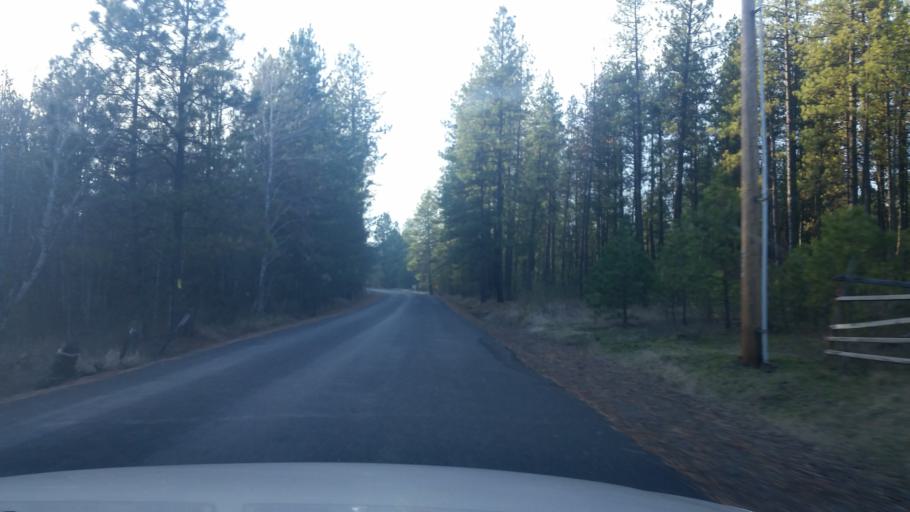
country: US
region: Washington
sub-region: Spokane County
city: Cheney
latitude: 47.5173
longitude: -117.4836
